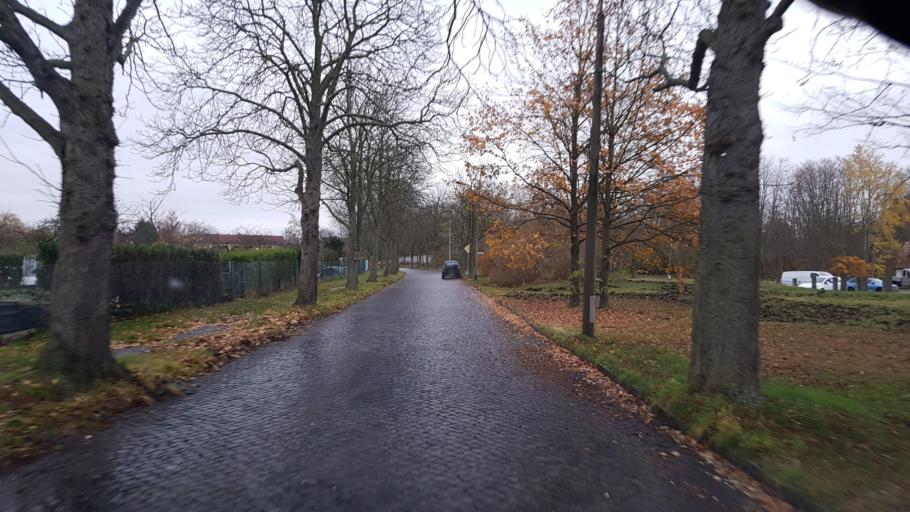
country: DE
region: Brandenburg
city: Lauchhammer
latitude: 51.4950
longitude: 13.7430
